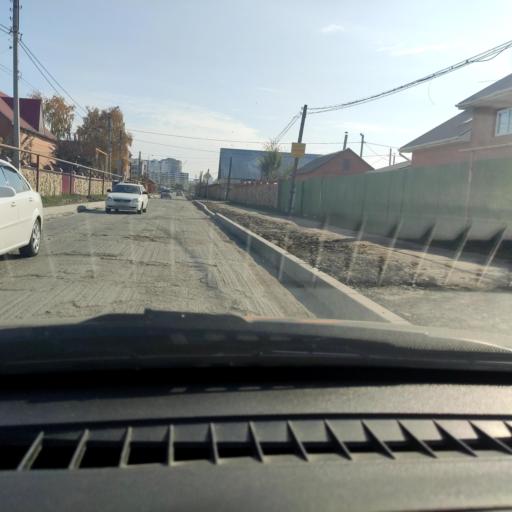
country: RU
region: Samara
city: Podstepki
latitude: 53.5113
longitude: 49.2368
